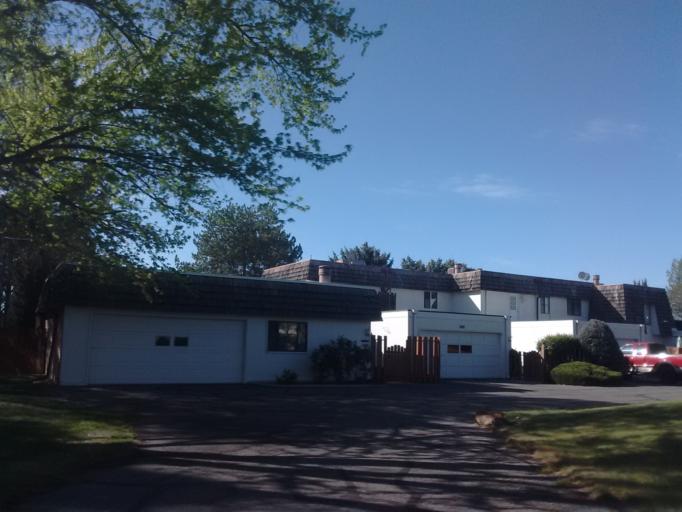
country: US
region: Colorado
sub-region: Mesa County
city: Grand Junction
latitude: 39.1081
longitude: -108.5517
